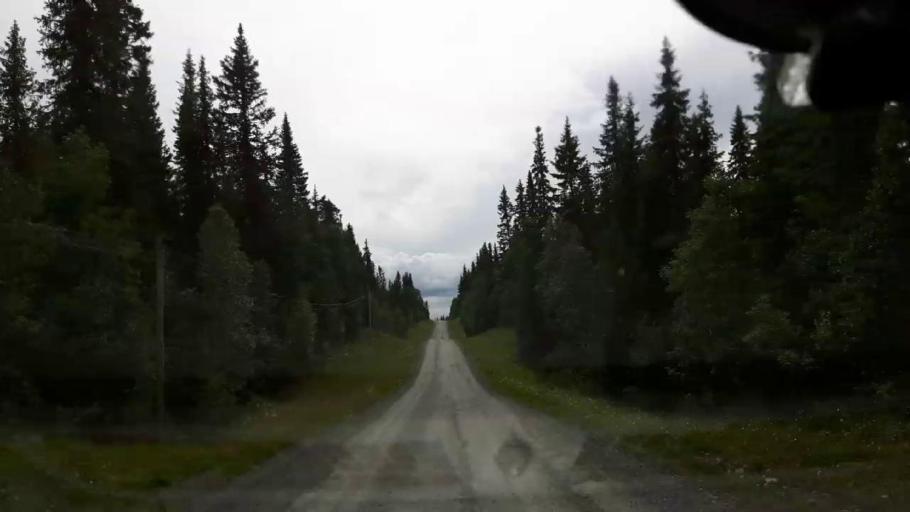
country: SE
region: Jaemtland
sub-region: Krokoms Kommun
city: Valla
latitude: 63.7460
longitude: 13.8357
